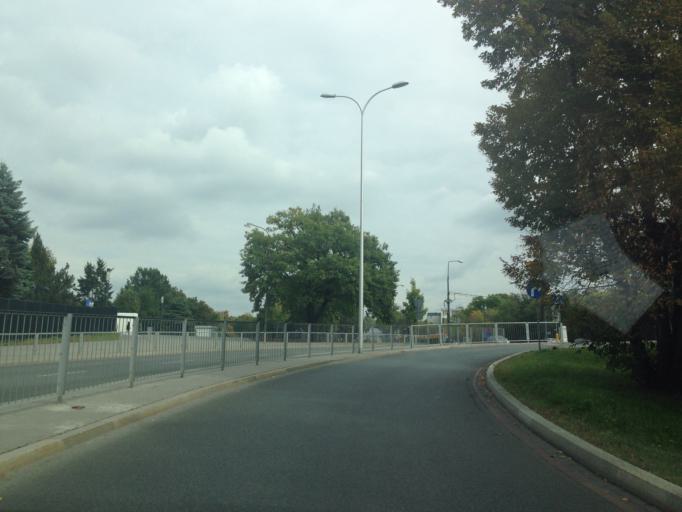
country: PL
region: Masovian Voivodeship
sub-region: Warszawa
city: Praga Polnoc
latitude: 52.2375
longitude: 21.0461
